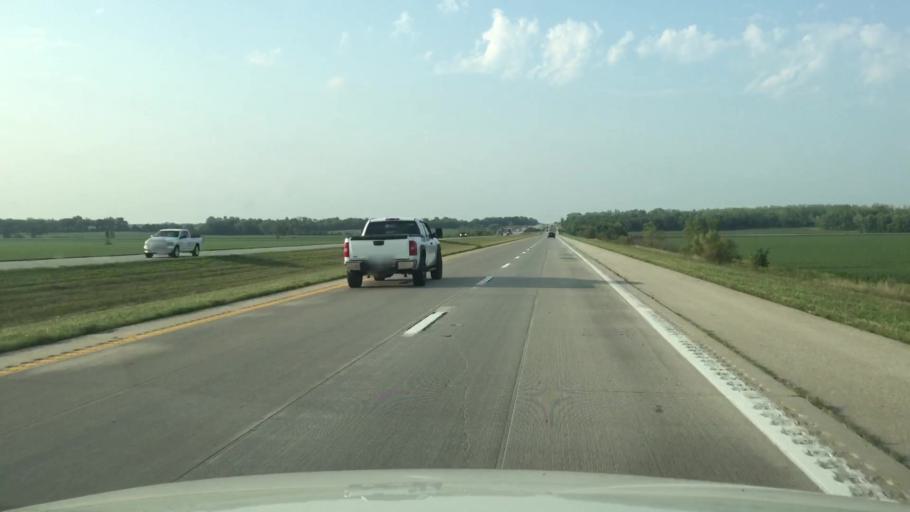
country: US
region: Missouri
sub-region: Daviess County
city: Gallatin
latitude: 40.0392
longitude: -94.0949
